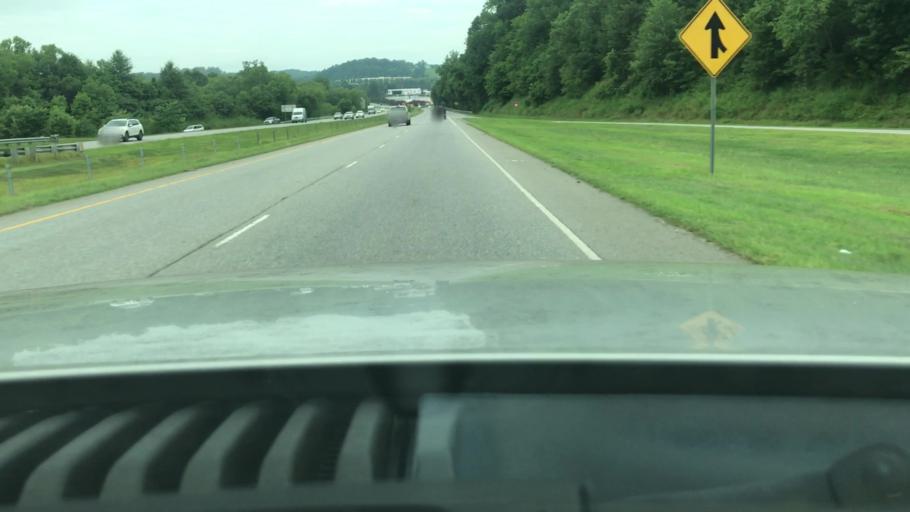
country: US
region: North Carolina
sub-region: Wilkes County
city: Wilkesboro
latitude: 36.1418
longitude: -81.1740
